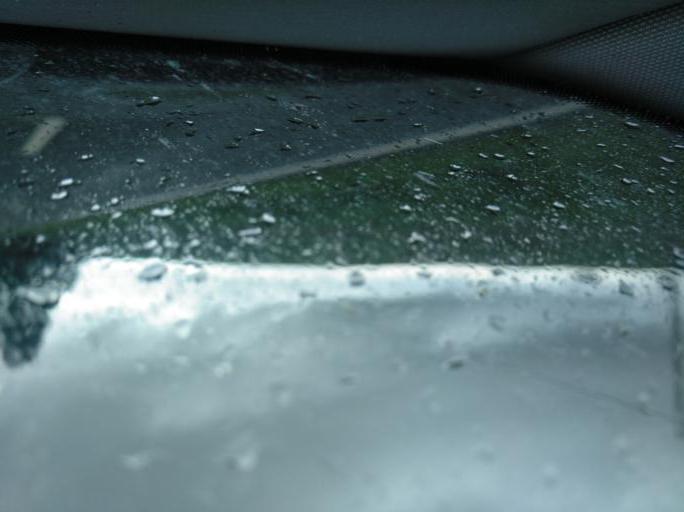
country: PT
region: Beja
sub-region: Aljustrel
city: Aljustrel
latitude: 37.8331
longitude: -8.1204
